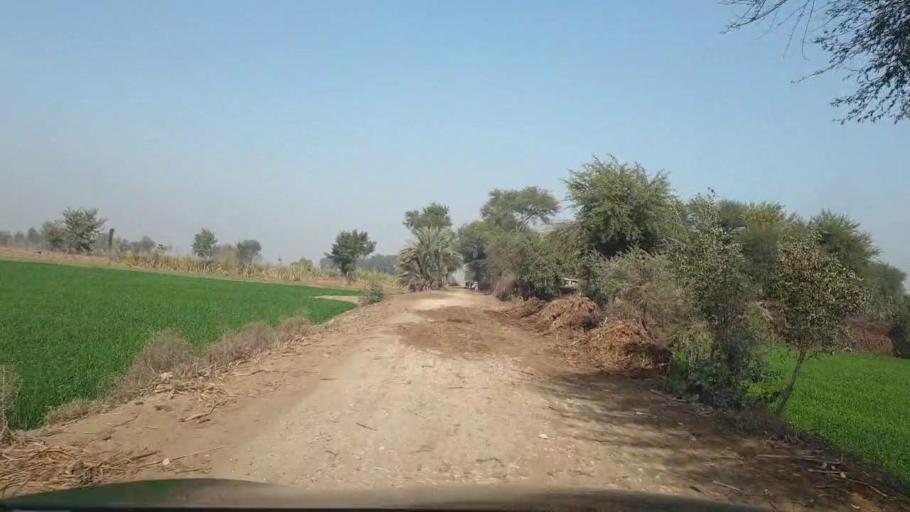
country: PK
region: Sindh
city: Ubauro
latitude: 28.1204
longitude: 69.7509
